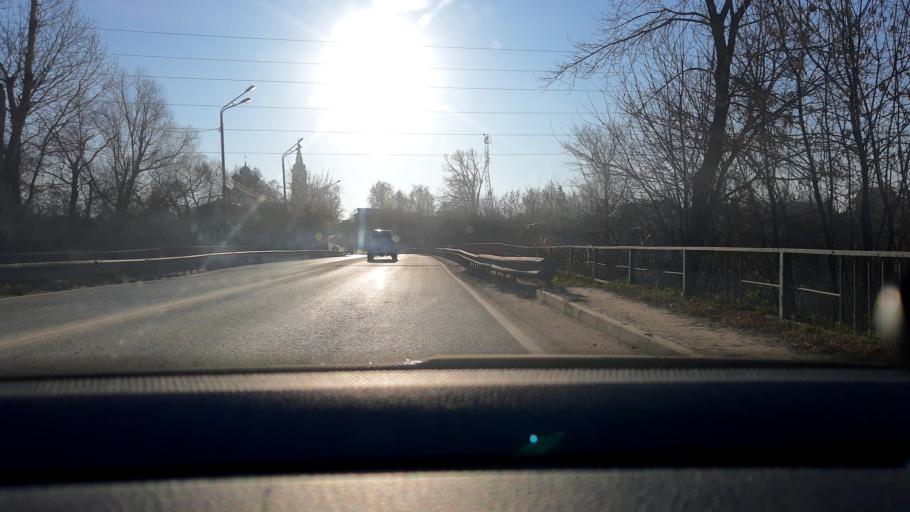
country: RU
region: Moskovskaya
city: Lesnyye Polyany
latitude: 55.9917
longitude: 37.8671
